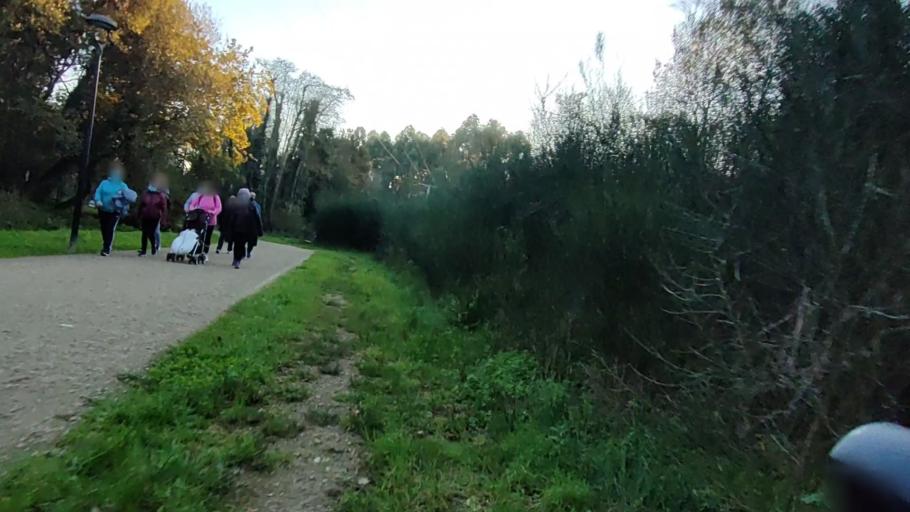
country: ES
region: Galicia
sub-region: Provincia da Coruna
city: Boiro
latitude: 42.6432
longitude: -8.8794
